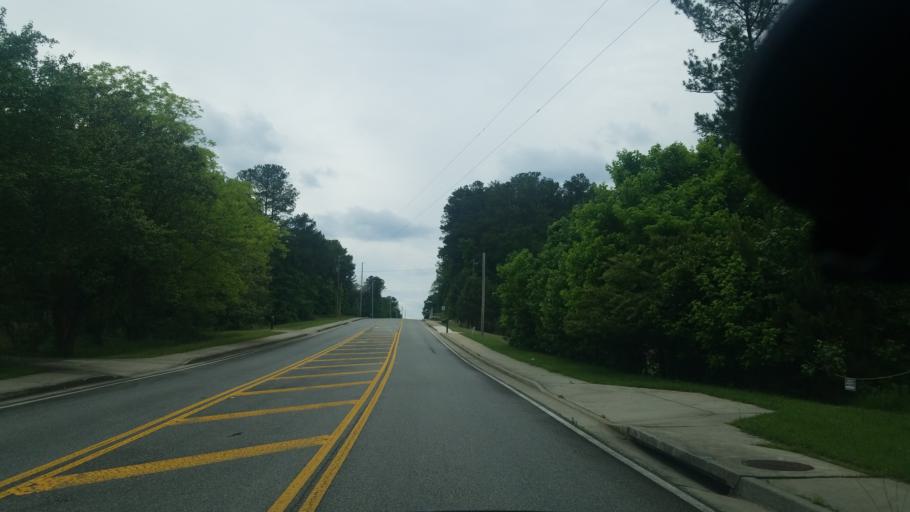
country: US
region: Georgia
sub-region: Forsyth County
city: Cumming
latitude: 34.1946
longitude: -84.1081
